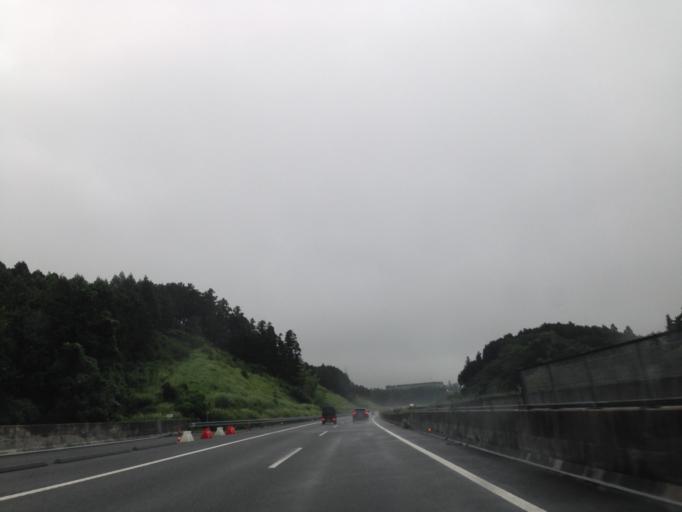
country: JP
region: Shizuoka
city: Gotemba
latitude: 35.2137
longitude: 138.8863
